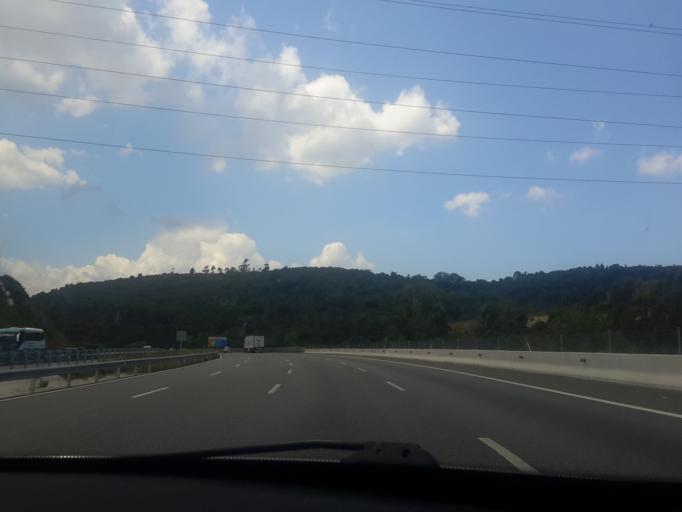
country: ES
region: Catalonia
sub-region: Provincia de Girona
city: Sant Julia de Ramis
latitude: 42.0436
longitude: 2.8461
